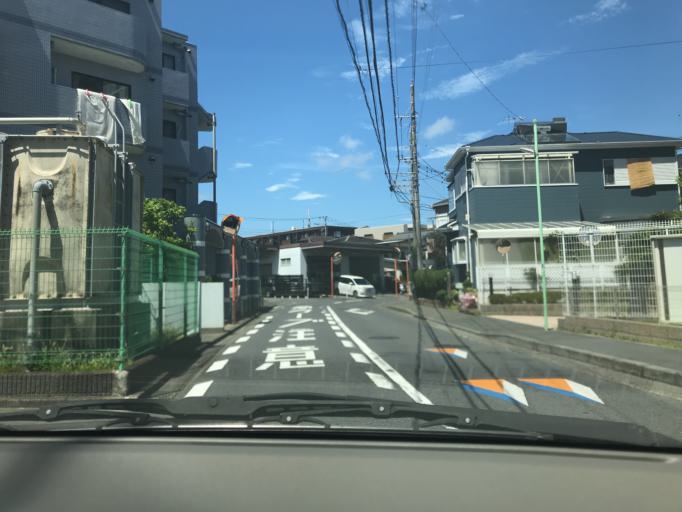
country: JP
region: Kanagawa
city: Fujisawa
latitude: 35.3503
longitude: 139.4669
